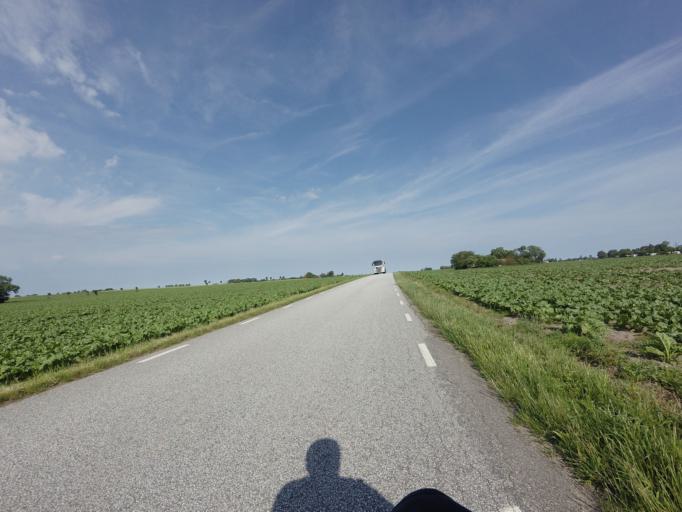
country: SE
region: Skane
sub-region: Vellinge Kommun
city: Vellinge
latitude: 55.4976
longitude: 13.0566
